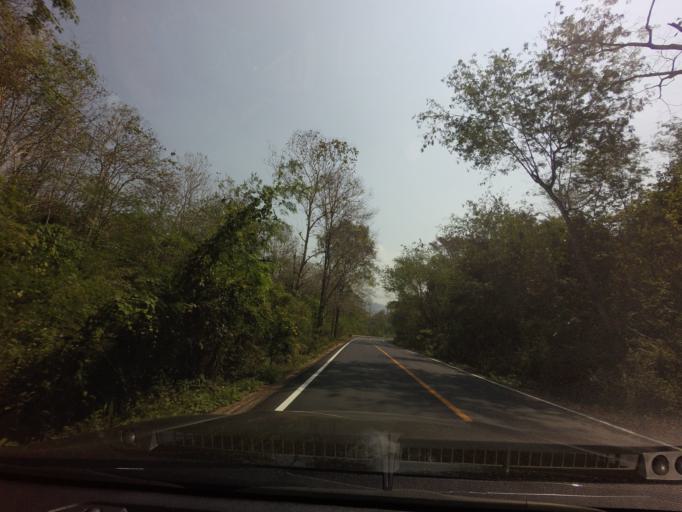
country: TH
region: Kanchanaburi
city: Thong Pha Phum
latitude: 14.7803
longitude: 98.5958
